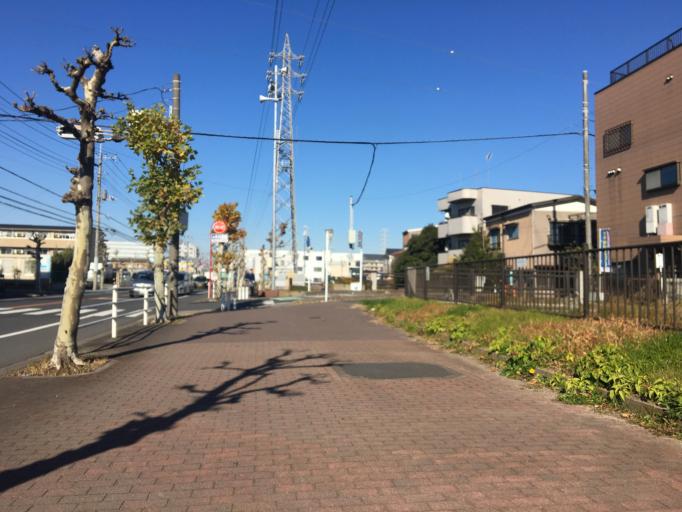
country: JP
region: Saitama
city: Yashio-shi
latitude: 35.8333
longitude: 139.8316
